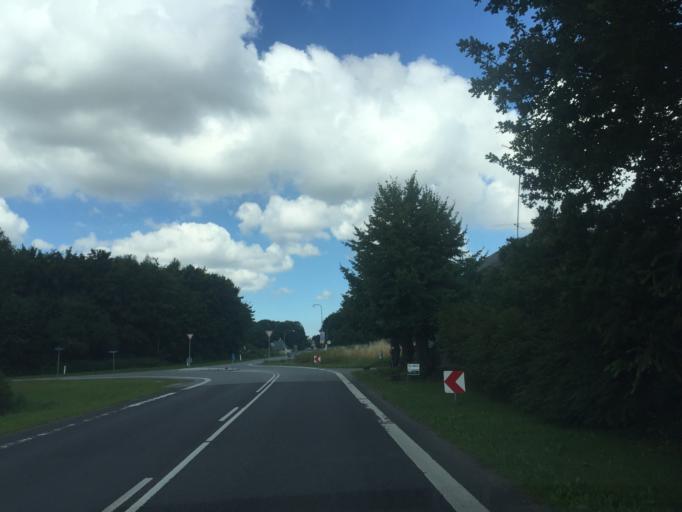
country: DK
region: South Denmark
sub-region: Nordfyns Kommune
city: Otterup
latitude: 55.5252
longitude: 10.3949
